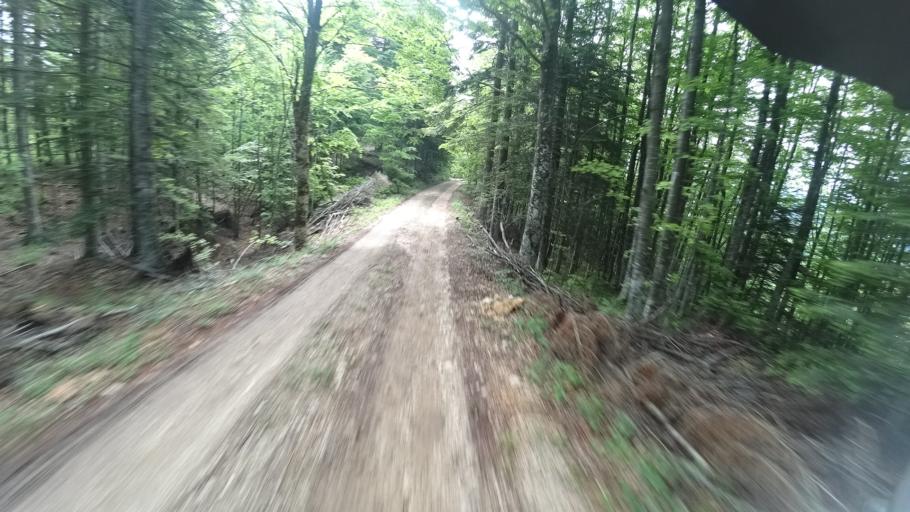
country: BA
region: Federation of Bosnia and Herzegovina
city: Bihac
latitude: 44.6797
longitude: 15.8452
